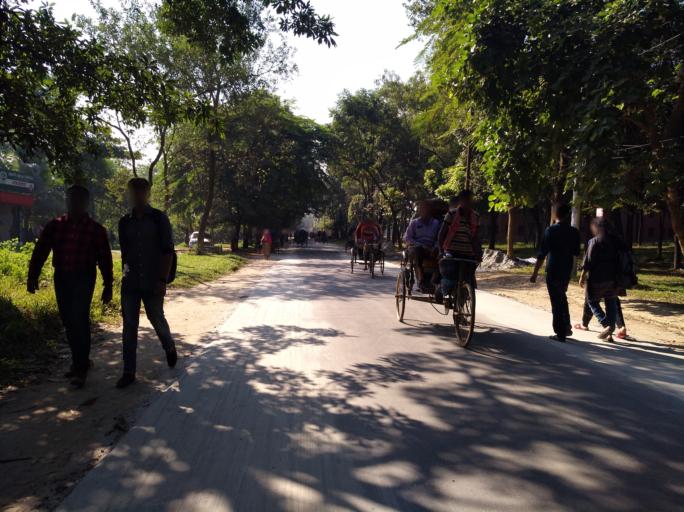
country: BD
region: Dhaka
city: Tungi
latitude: 23.8823
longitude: 90.2678
